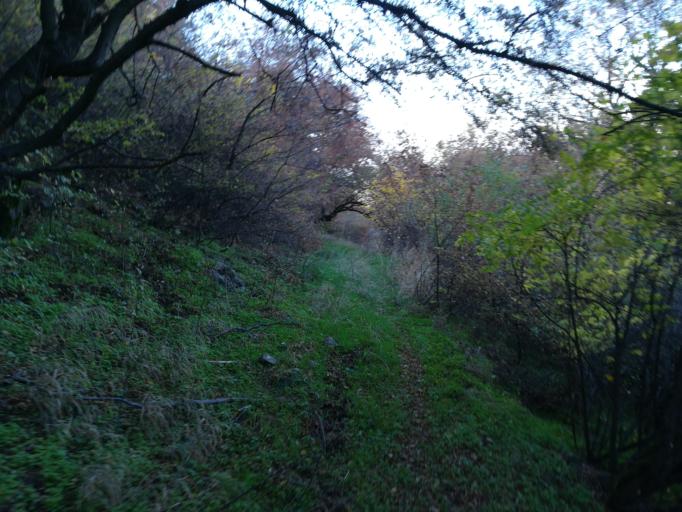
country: BG
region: Khaskovo
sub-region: Obshtina Mineralni Bani
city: Mineralni Bani
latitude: 41.9807
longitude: 25.2389
